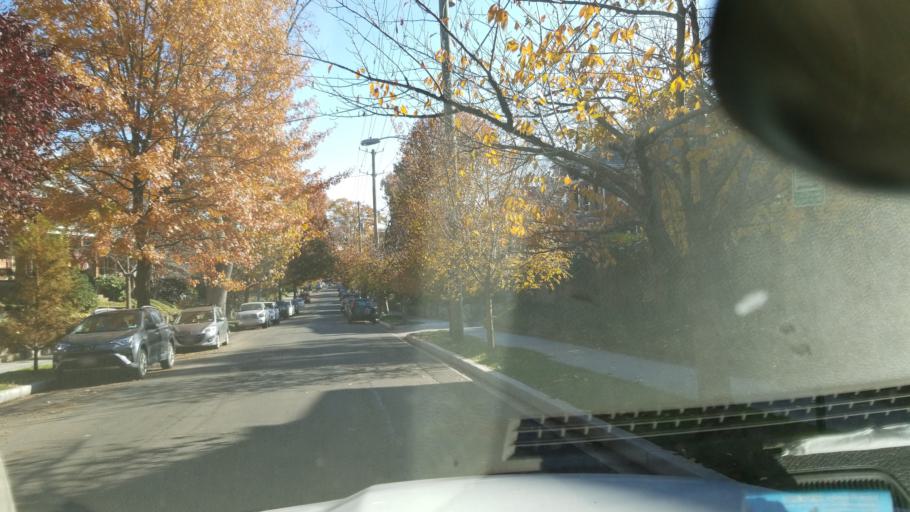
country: US
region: Maryland
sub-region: Montgomery County
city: Friendship Village
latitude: 38.9448
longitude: -77.0746
